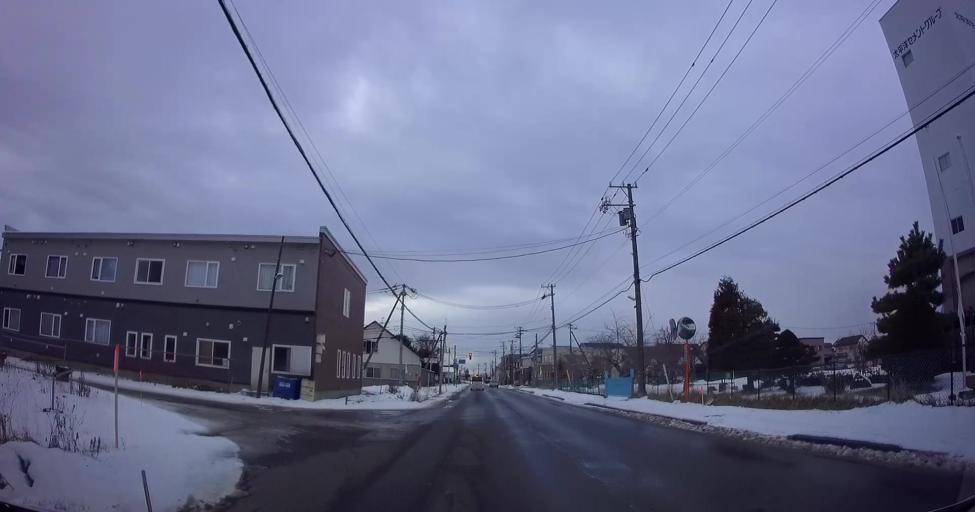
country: JP
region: Hokkaido
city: Kamiiso
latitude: 41.8291
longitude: 140.6871
